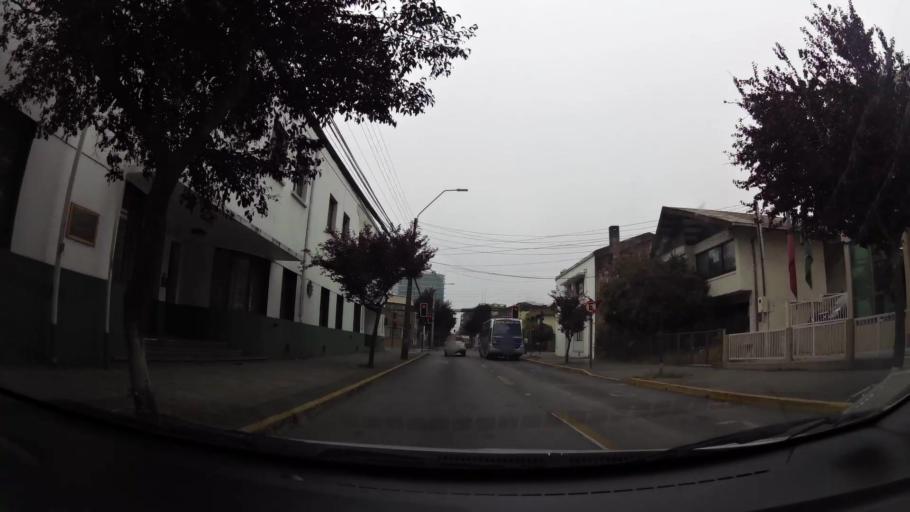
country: CL
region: Biobio
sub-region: Provincia de Concepcion
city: Concepcion
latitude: -36.8311
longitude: -73.0554
